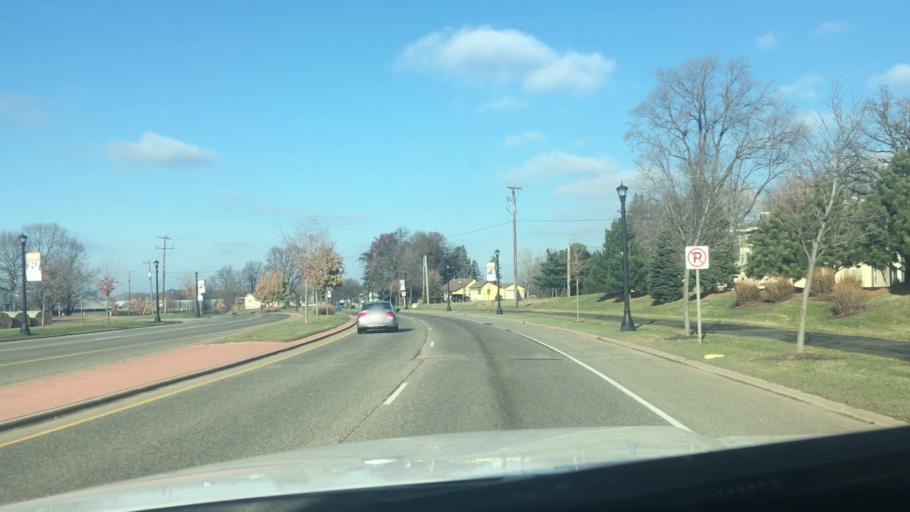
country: US
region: Minnesota
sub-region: Washington County
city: Hugo
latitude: 45.1593
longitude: -92.9986
